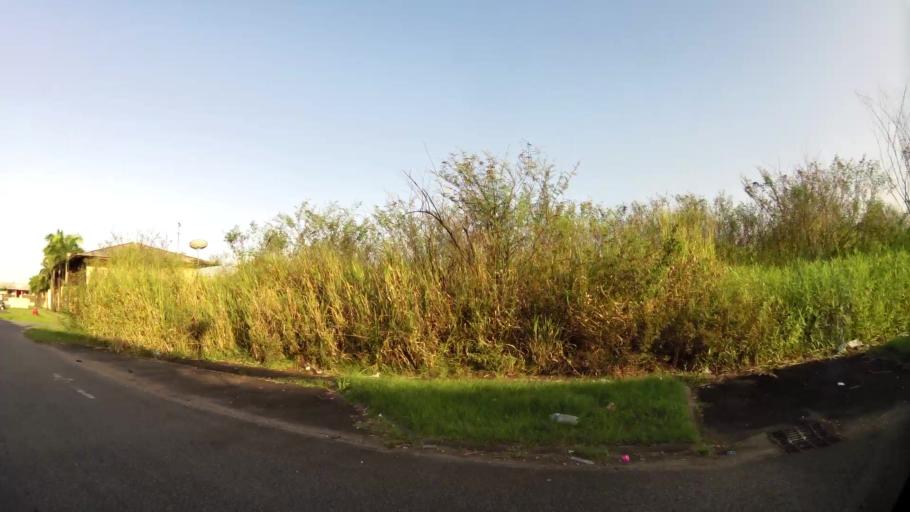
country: GF
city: Macouria
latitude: 5.0116
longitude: -52.4778
